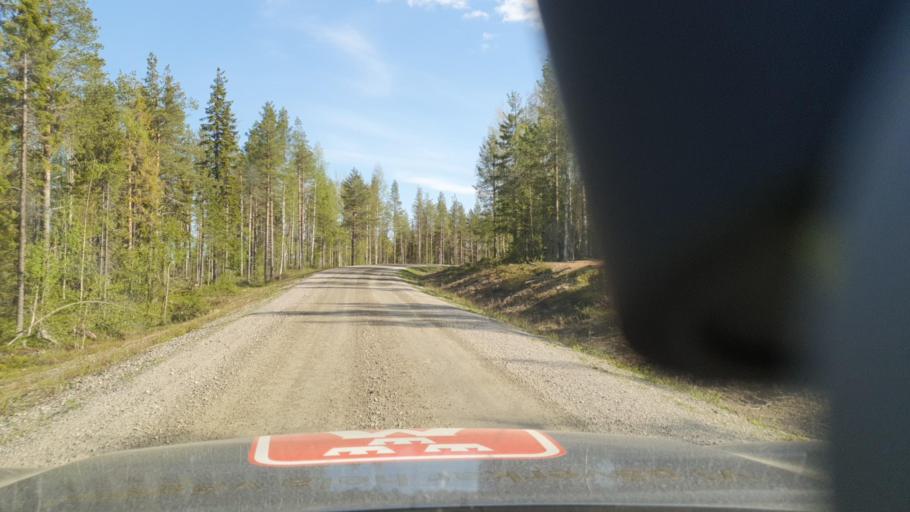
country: SE
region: Norrbotten
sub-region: Bodens Kommun
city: Boden
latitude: 66.4603
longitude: 21.8662
